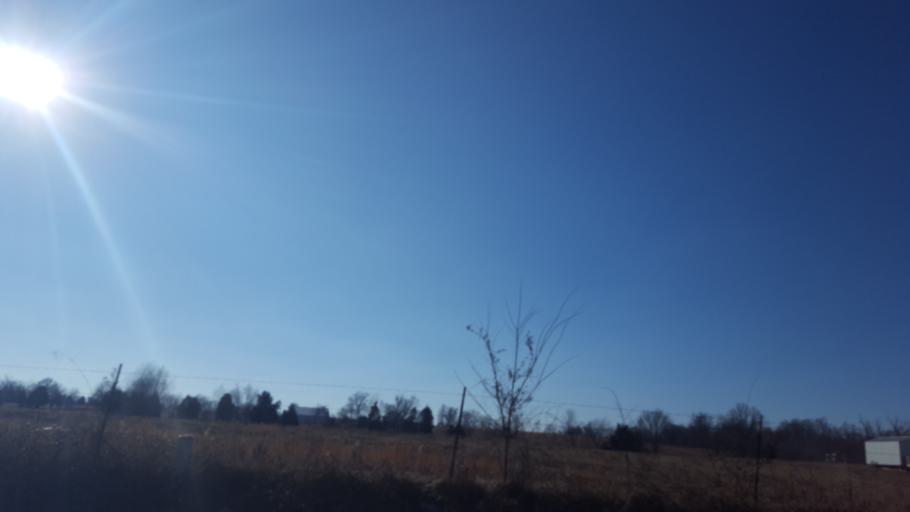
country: US
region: Kentucky
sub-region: Crittenden County
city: Marion
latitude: 37.4313
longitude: -88.0469
